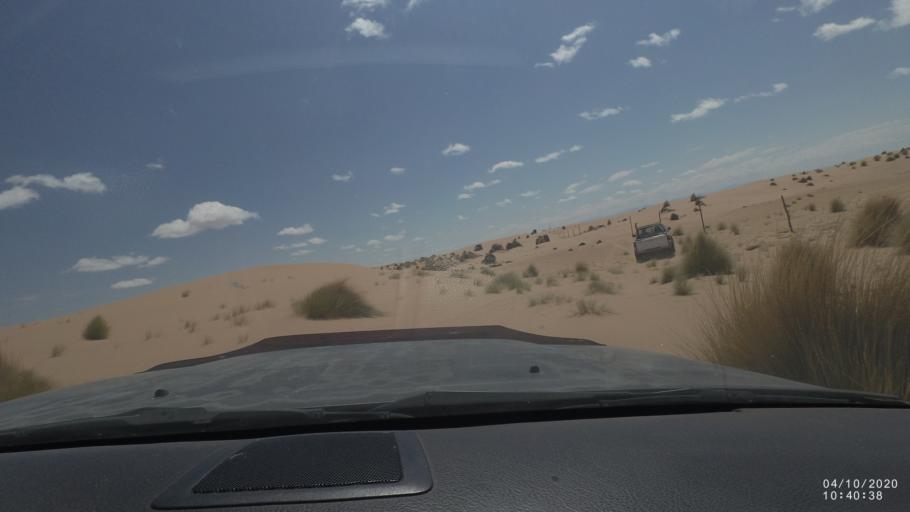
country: BO
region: Oruro
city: Poopo
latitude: -18.7054
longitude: -67.4725
